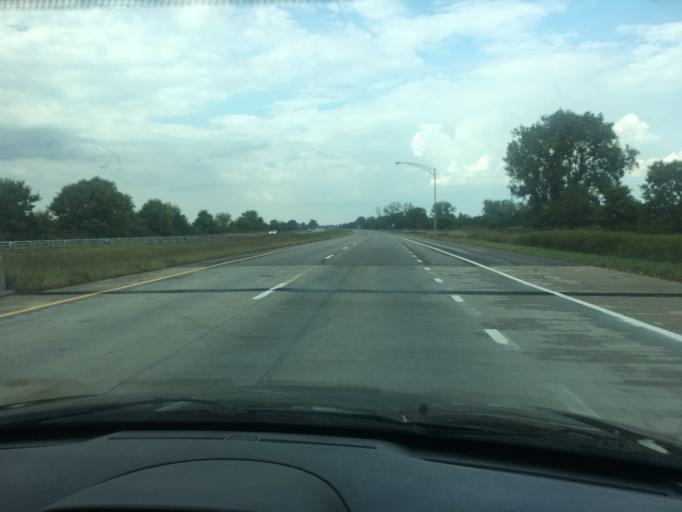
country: US
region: Ohio
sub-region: Clark County
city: Northridge
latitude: 39.9928
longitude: -83.8114
